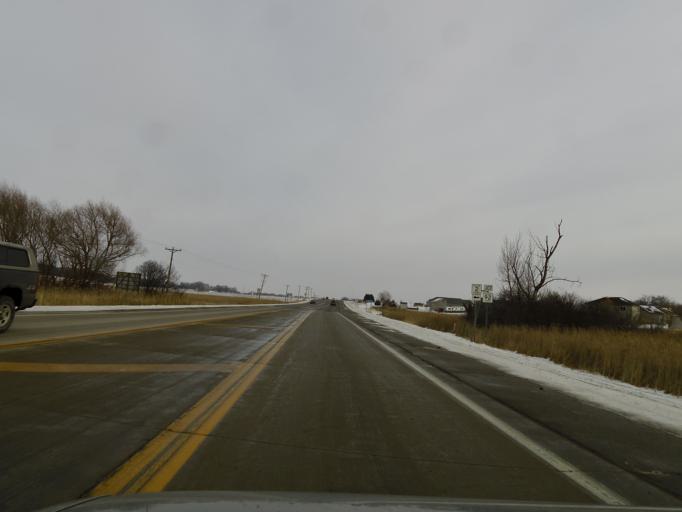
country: US
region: Minnesota
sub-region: McLeod County
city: Glencoe
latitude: 44.9069
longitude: -94.1914
